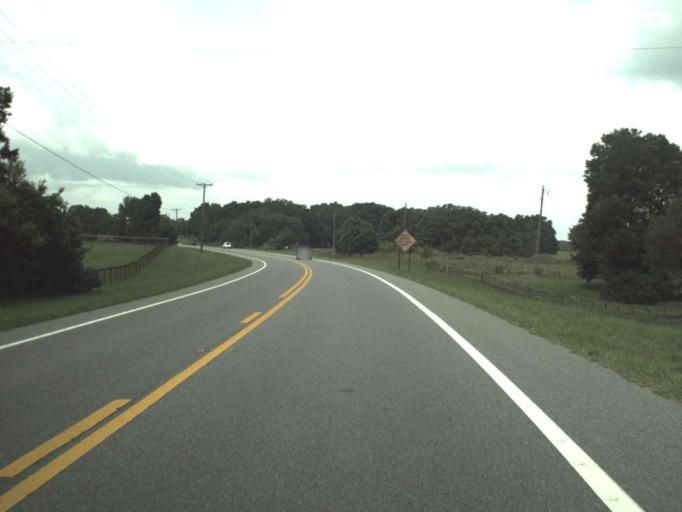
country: US
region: Florida
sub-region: Sumter County
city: Lake Panasoffkee
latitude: 28.7255
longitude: -82.0826
